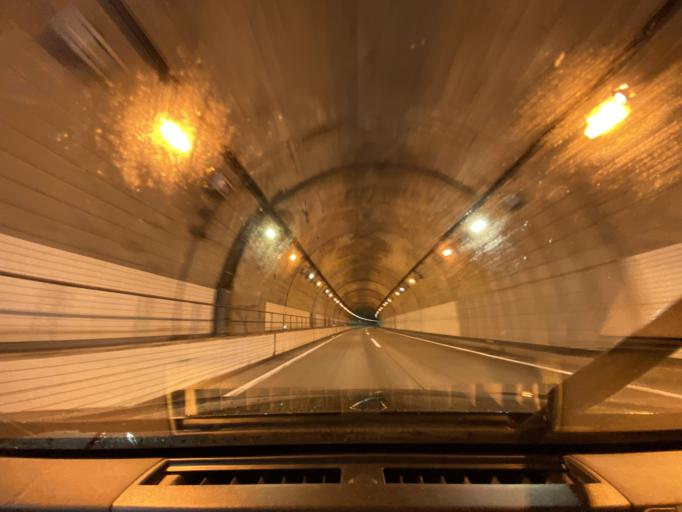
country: JP
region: Hokkaido
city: Bibai
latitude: 43.3075
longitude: 141.8813
